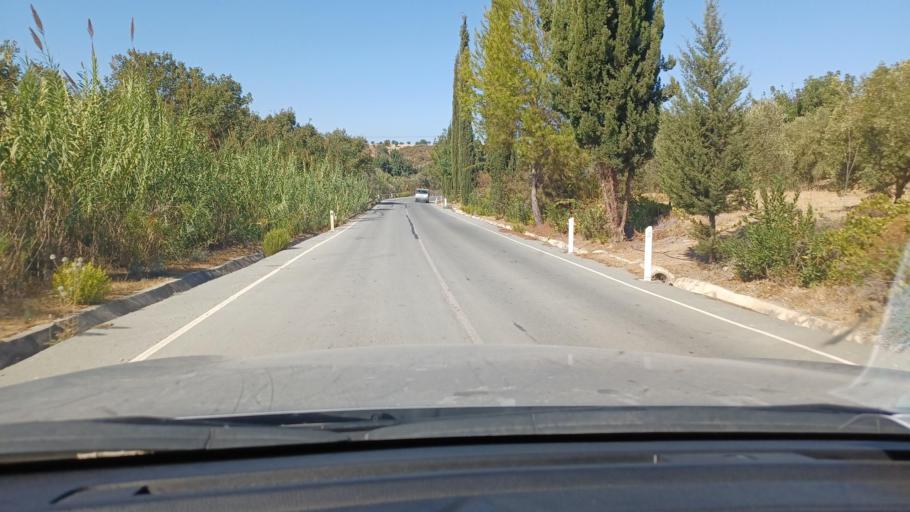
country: CY
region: Pafos
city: Polis
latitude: 35.0028
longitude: 32.4654
